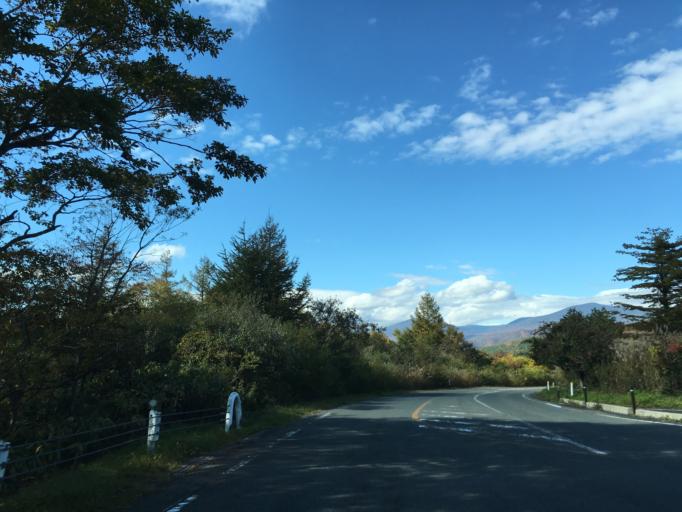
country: JP
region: Fukushima
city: Inawashiro
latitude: 37.5947
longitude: 140.2416
